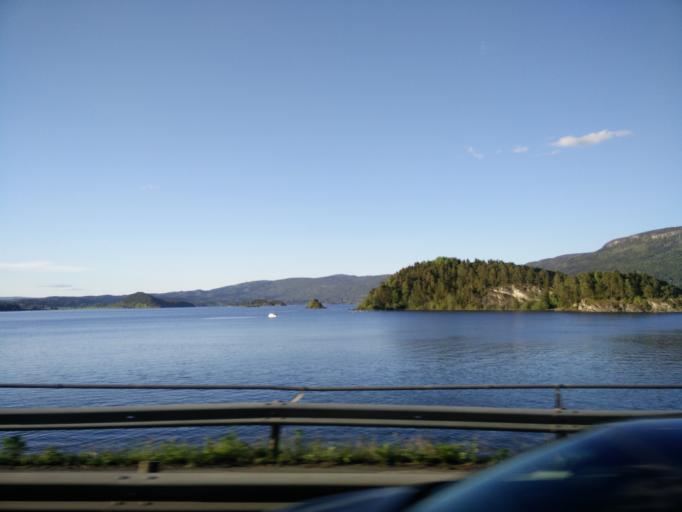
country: NO
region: Buskerud
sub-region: Hole
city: Vik
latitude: 60.0756
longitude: 10.2978
